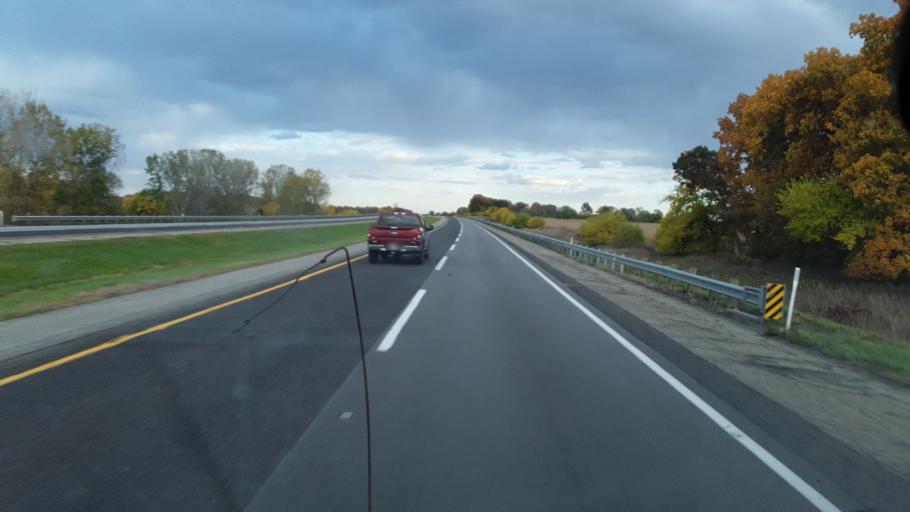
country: US
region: Indiana
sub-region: Steuben County
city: Angola
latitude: 41.7482
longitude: -85.0845
